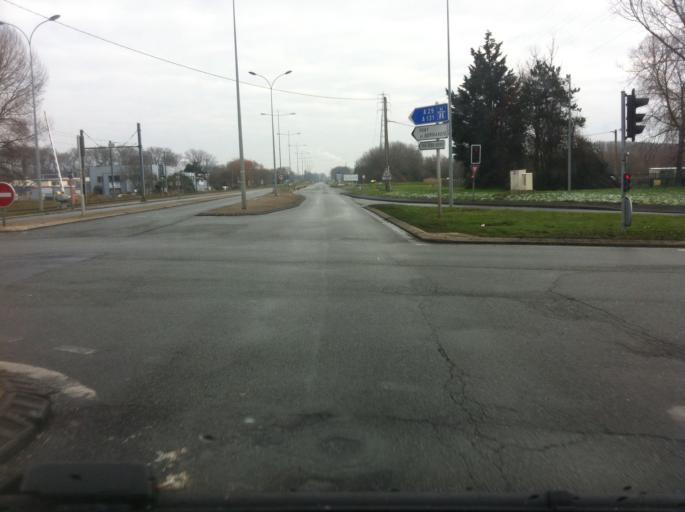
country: FR
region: Haute-Normandie
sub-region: Departement de la Seine-Maritime
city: Harfleur
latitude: 49.4878
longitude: 0.1872
